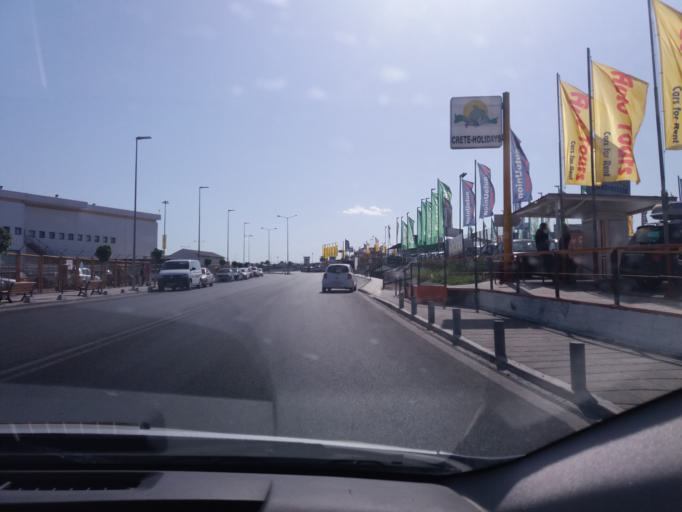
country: GR
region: Crete
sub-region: Nomos Irakleiou
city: Nea Alikarnassos
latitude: 35.3376
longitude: 25.1717
